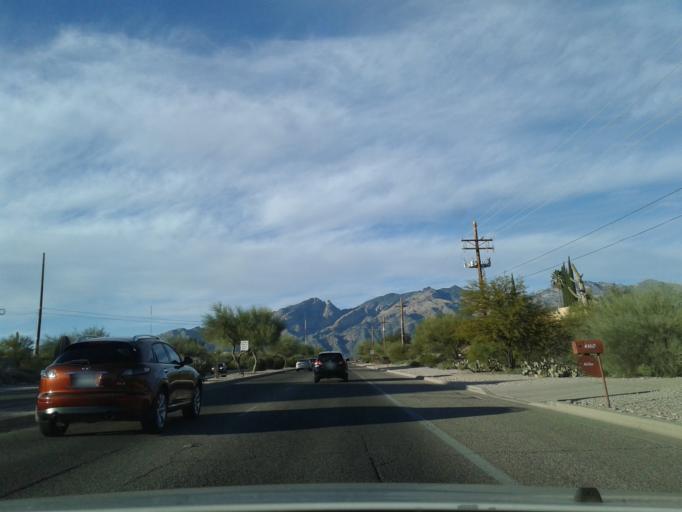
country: US
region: Arizona
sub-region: Pima County
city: Catalina Foothills
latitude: 32.2824
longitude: -110.8925
